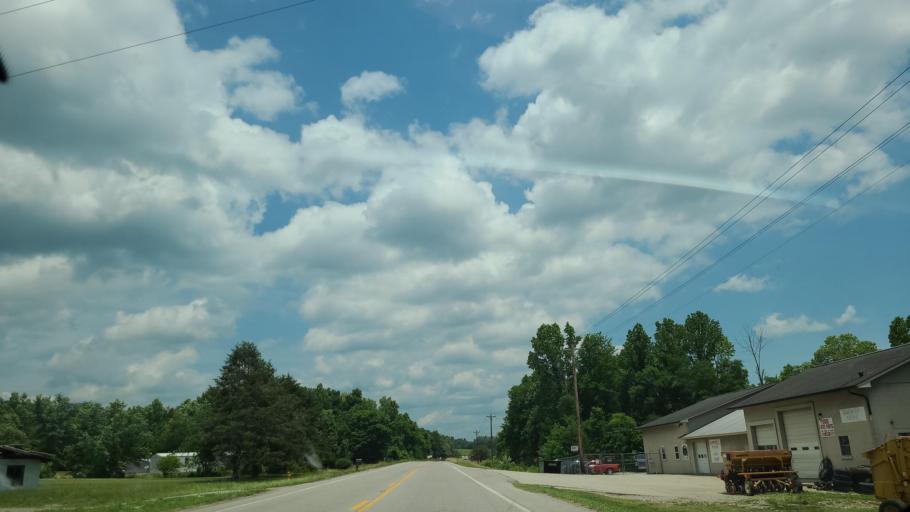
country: US
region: Tennessee
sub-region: Bledsoe County
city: Pikeville
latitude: 35.6453
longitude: -85.1660
